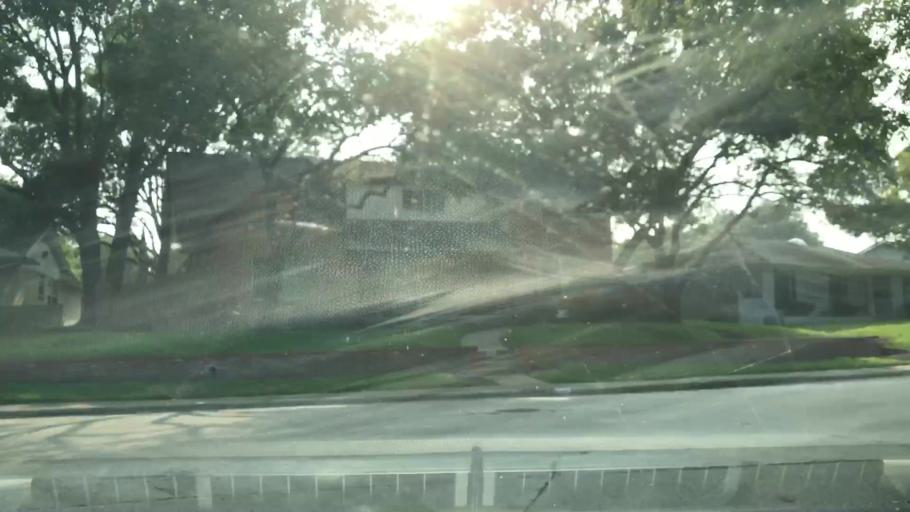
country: US
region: Texas
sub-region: Dallas County
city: Richardson
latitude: 32.9048
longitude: -96.7326
